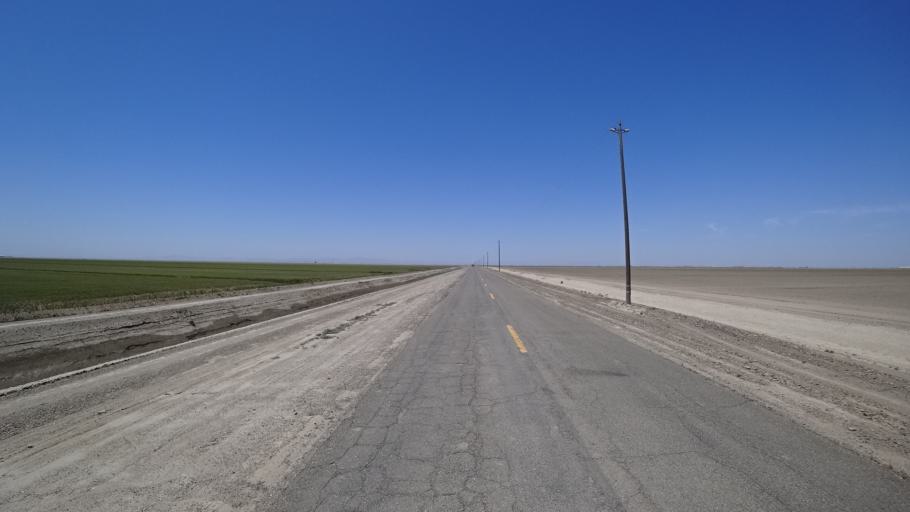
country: US
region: California
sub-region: Kings County
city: Corcoran
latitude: 36.1162
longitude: -119.6583
